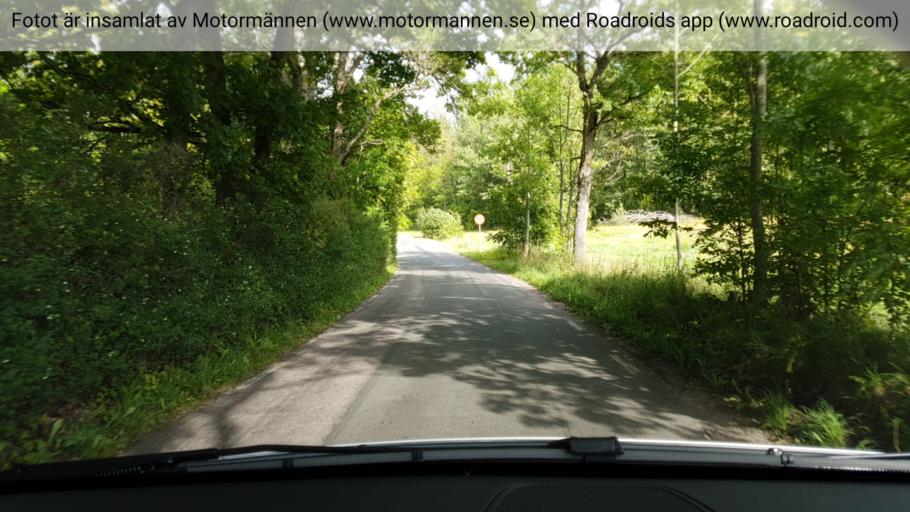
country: SE
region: Vaestra Goetaland
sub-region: Skovde Kommun
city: Skultorp
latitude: 58.2895
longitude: 13.8248
